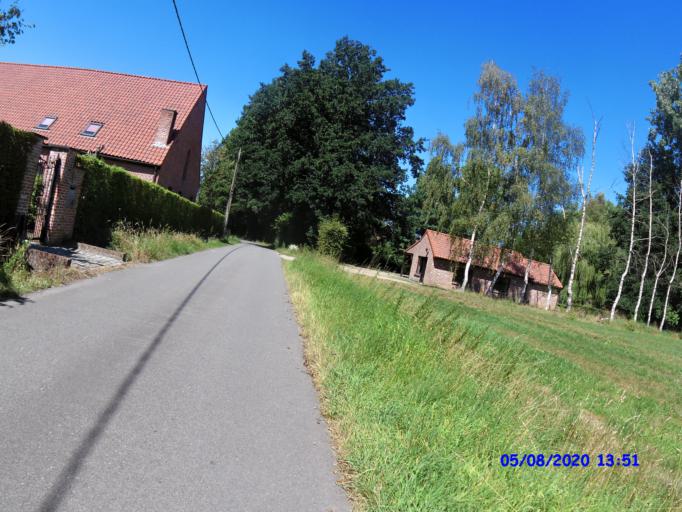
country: BE
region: Flanders
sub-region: Provincie Antwerpen
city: Hoogstraten
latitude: 51.3817
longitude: 4.7860
